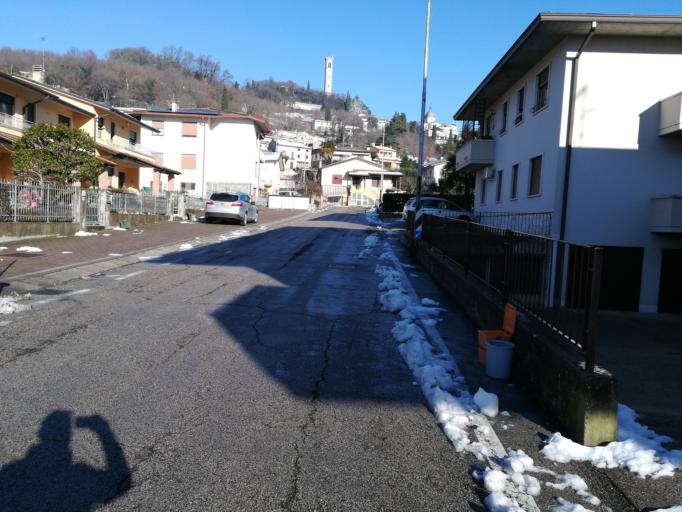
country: IT
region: Veneto
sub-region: Provincia di Vicenza
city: Trissino
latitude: 45.5635
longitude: 11.3661
